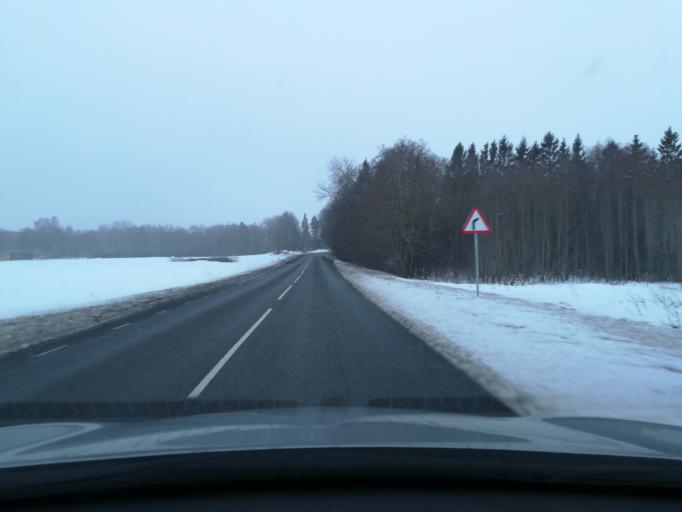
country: EE
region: Harju
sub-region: Raasiku vald
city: Arukula
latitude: 59.3476
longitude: 25.1255
